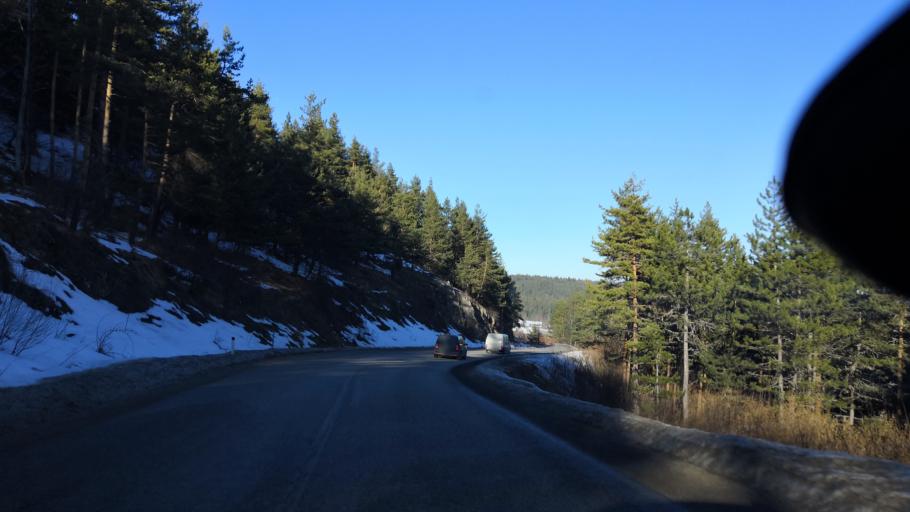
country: BA
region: Republika Srpska
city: Sokolac
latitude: 43.9130
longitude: 18.7195
